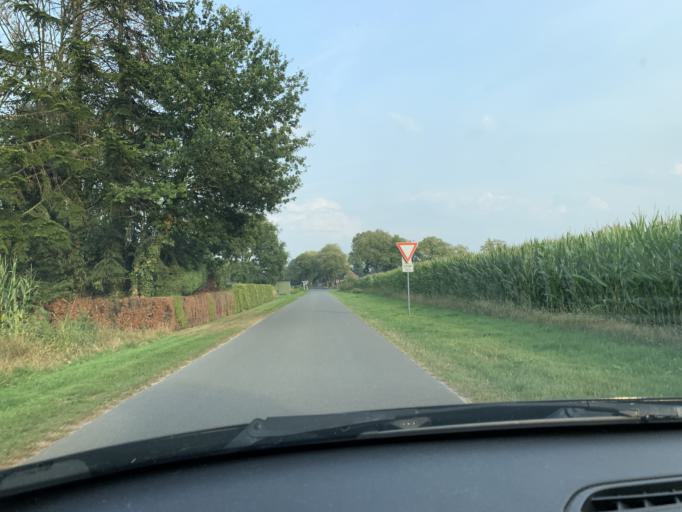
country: DE
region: Lower Saxony
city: Westerstede
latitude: 53.2573
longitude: 7.8911
